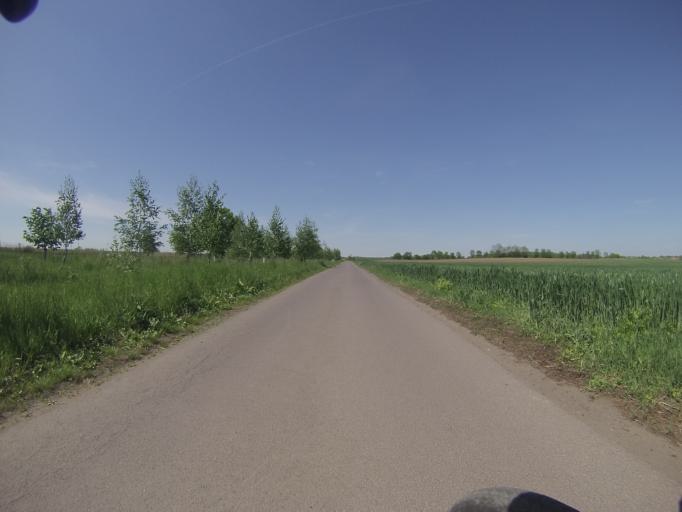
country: CZ
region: South Moravian
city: Novosedly
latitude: 48.8077
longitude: 16.4862
